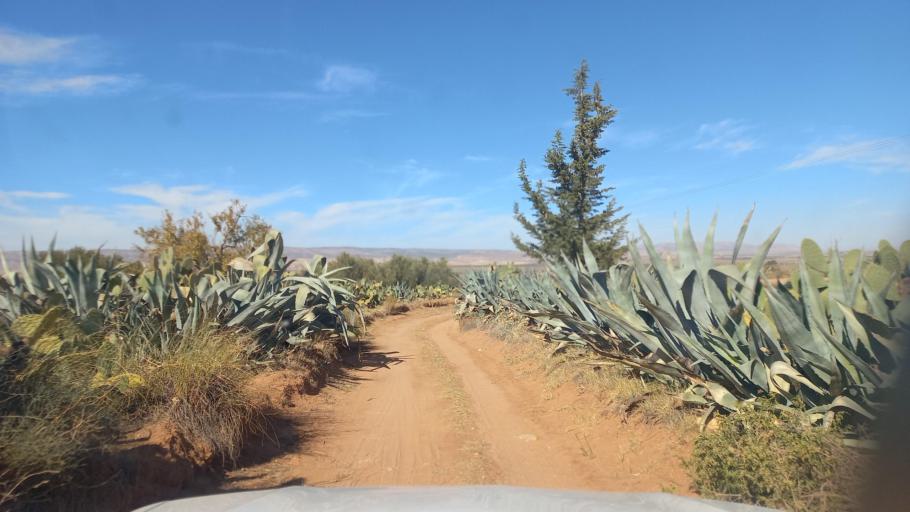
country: TN
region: Al Qasrayn
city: Kasserine
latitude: 35.2033
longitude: 8.9704
